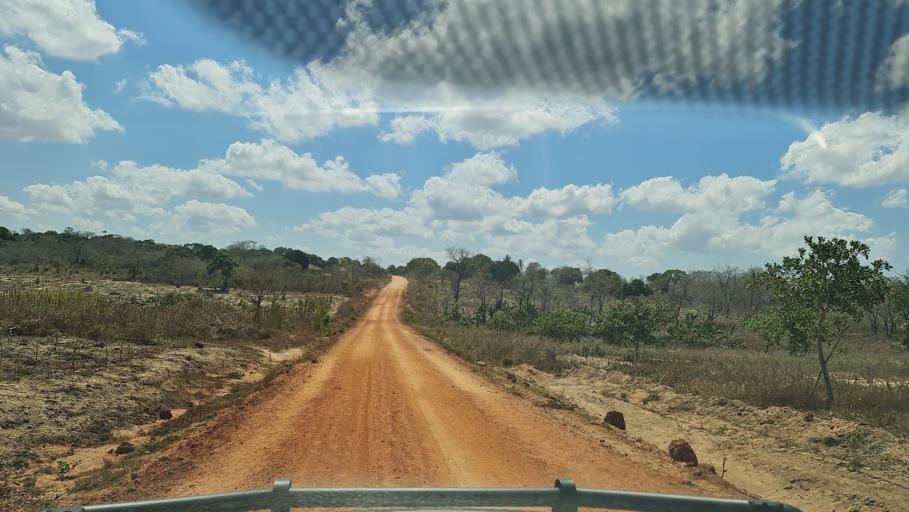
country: MZ
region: Nampula
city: Nacala
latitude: -14.1754
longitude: 40.2336
